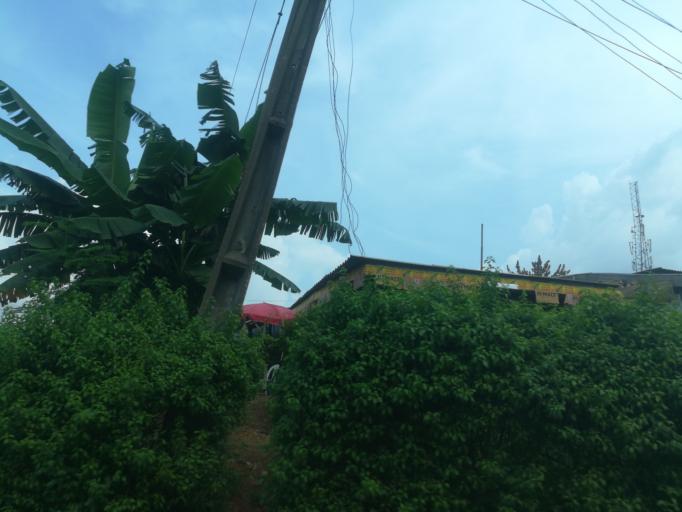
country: NG
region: Oyo
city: Ibadan
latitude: 7.3671
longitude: 3.8526
